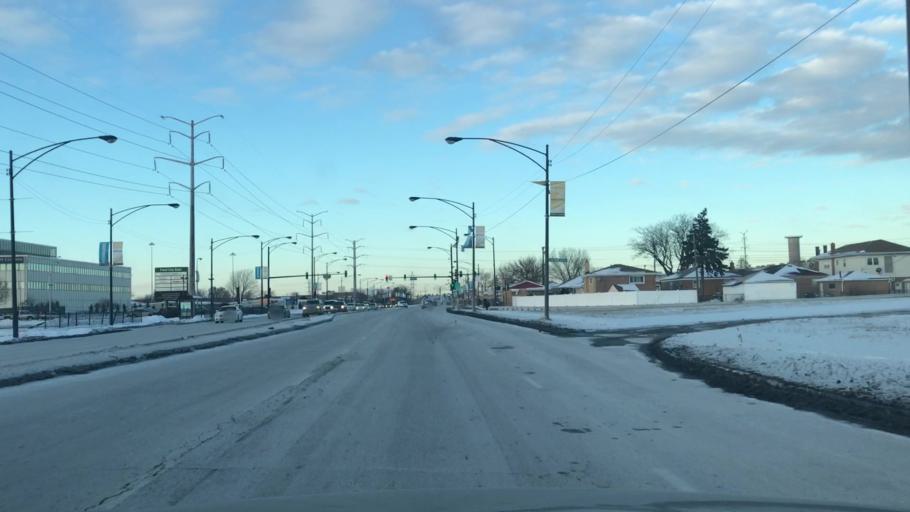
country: US
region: Illinois
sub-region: Cook County
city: Hometown
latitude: 41.7537
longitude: -87.7220
